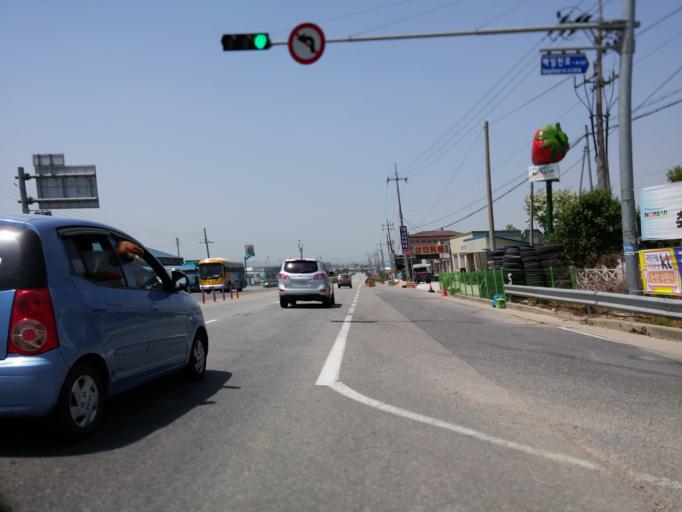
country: KR
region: Chungcheongnam-do
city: Nonsan
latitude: 36.2130
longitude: 127.1432
